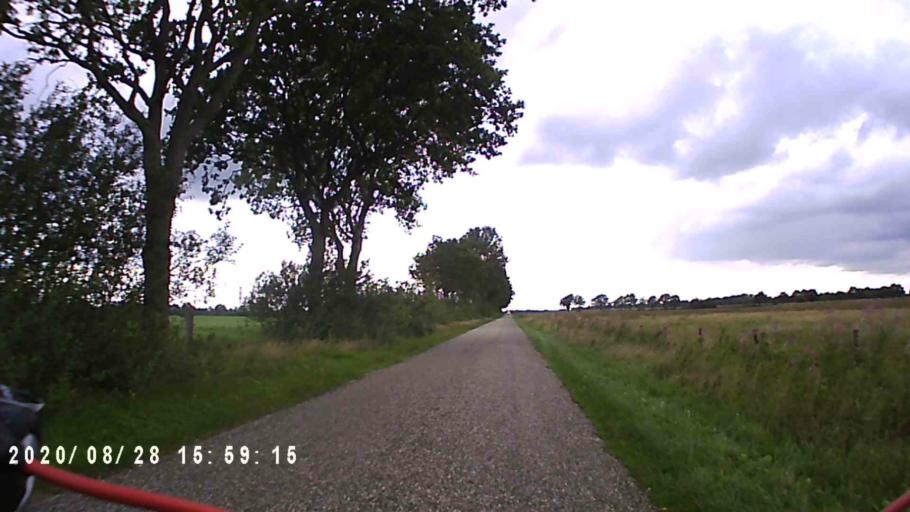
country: NL
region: Drenthe
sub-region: Gemeente Tynaarlo
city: Vries
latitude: 53.1067
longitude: 6.5129
